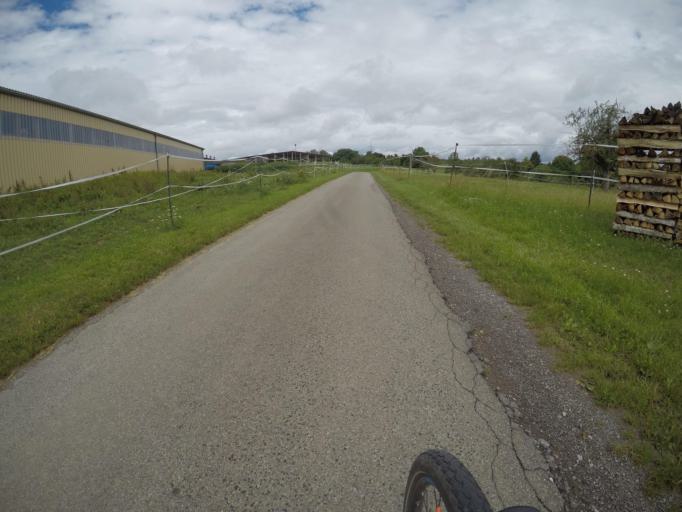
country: DE
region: Baden-Wuerttemberg
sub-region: Regierungsbezirk Stuttgart
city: Gartringen
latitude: 48.6460
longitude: 8.8840
